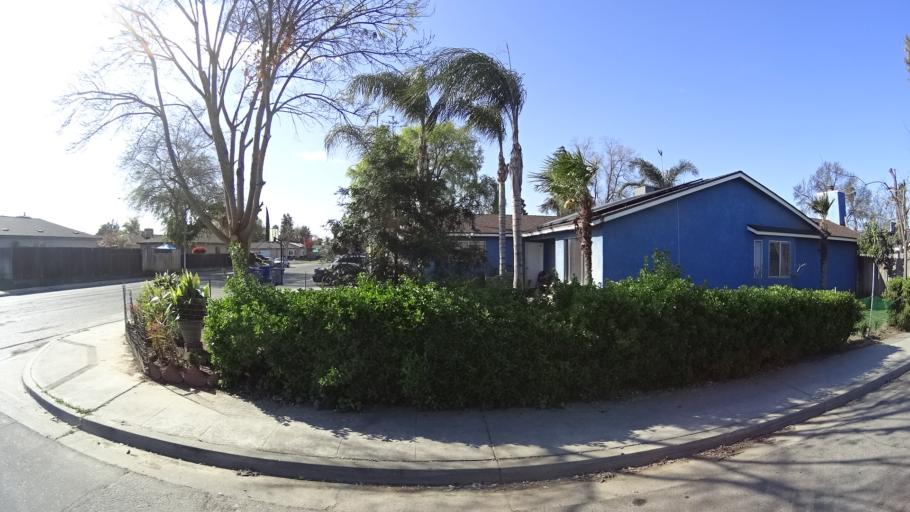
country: US
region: California
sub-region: Fresno County
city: West Park
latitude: 36.7987
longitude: -119.8829
